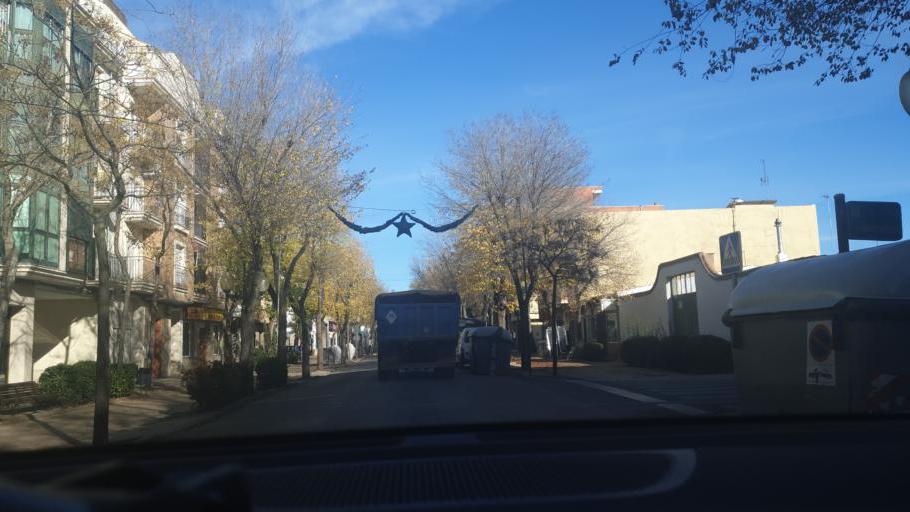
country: ES
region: Castille-La Mancha
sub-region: Provincia de Ciudad Real
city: Tomelloso
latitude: 39.1501
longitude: -3.0181
